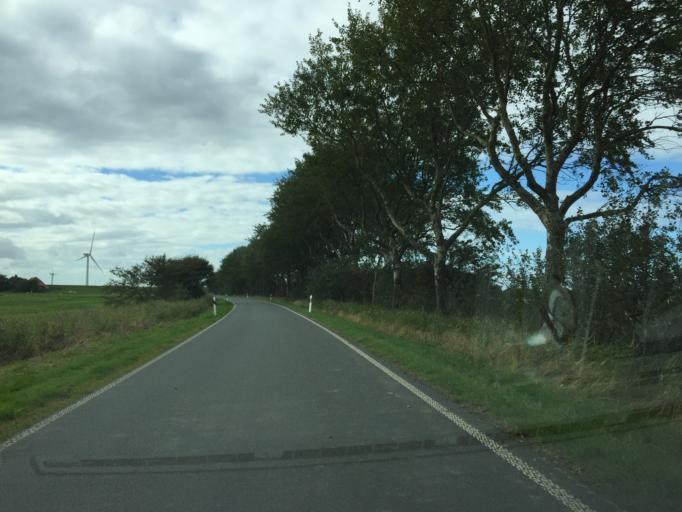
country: DE
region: Schleswig-Holstein
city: Friedrich-Wilhelm-Lubke-Koog
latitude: 54.8364
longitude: 8.6541
